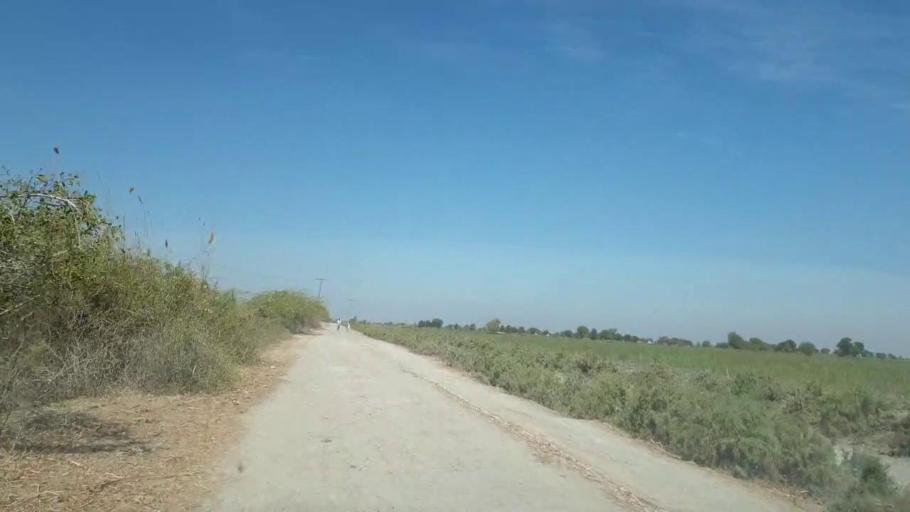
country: PK
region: Sindh
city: Pithoro
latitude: 25.6114
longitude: 69.2165
